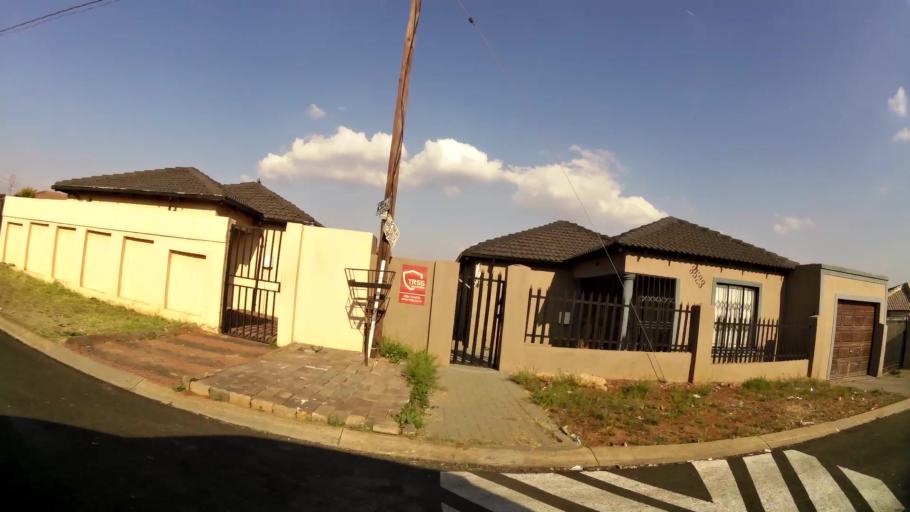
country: ZA
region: Gauteng
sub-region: Ekurhuleni Metropolitan Municipality
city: Tembisa
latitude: -25.9566
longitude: 28.2155
